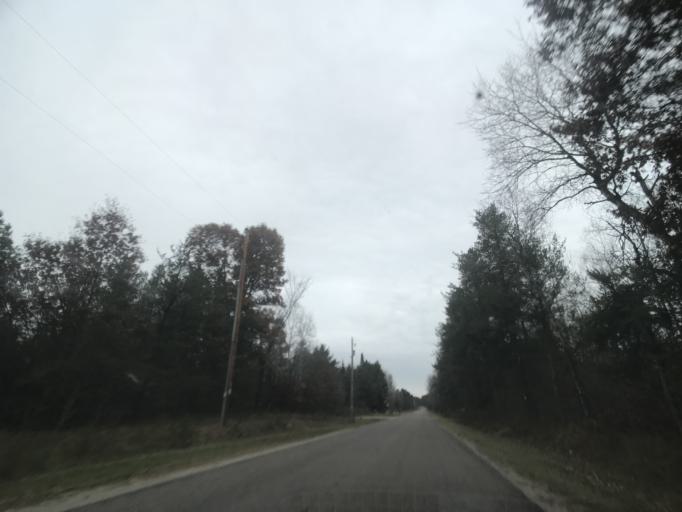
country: US
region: Wisconsin
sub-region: Oconto County
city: Gillett
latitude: 45.2785
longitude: -88.2571
